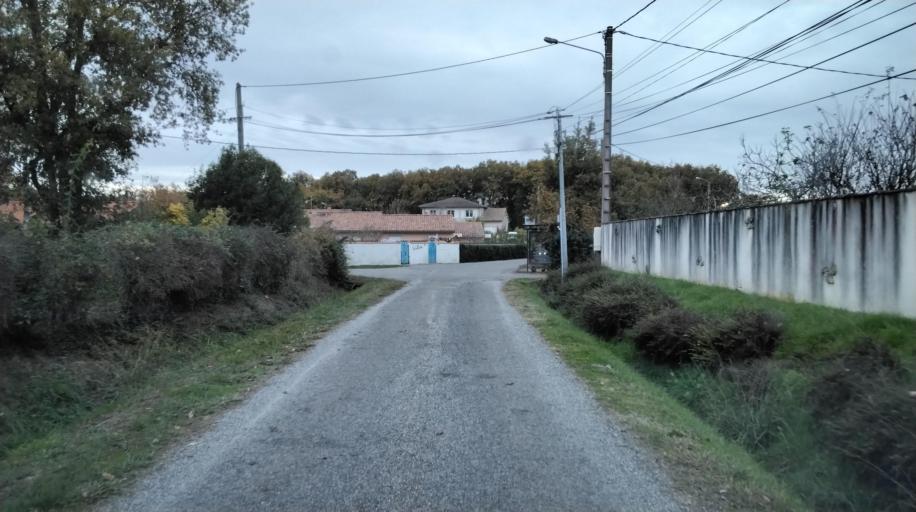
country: FR
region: Midi-Pyrenees
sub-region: Departement de la Haute-Garonne
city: Berat
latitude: 43.3934
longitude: 1.2051
